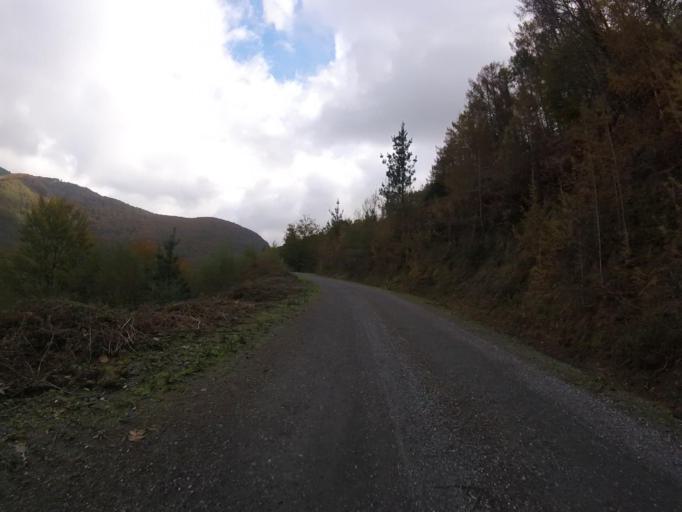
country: ES
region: Navarre
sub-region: Provincia de Navarra
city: Goizueta
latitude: 43.2253
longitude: -1.8266
